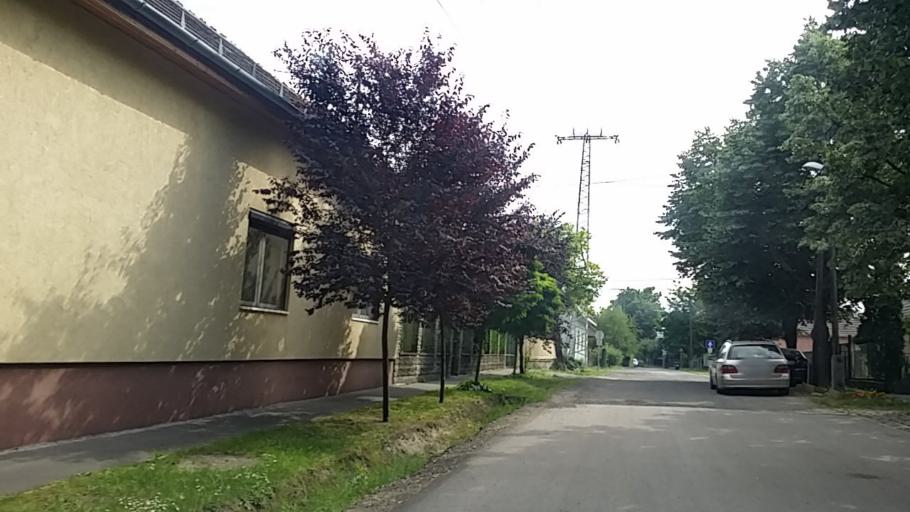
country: HU
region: Budapest
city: Budapest XXI. keruelet
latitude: 47.4120
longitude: 19.0712
